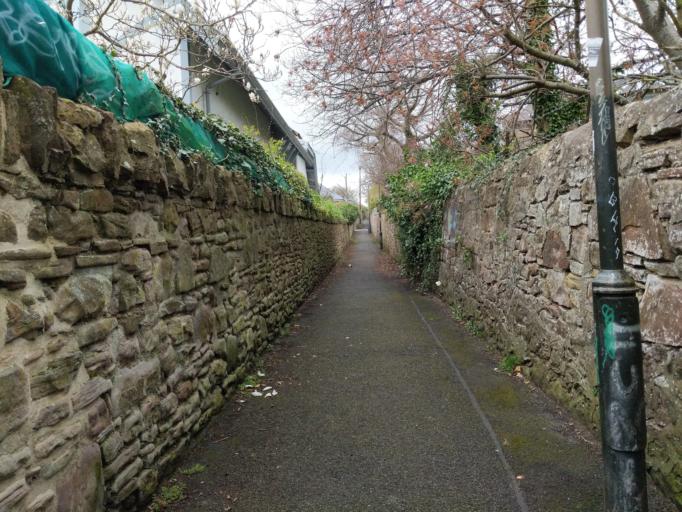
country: GB
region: Scotland
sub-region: Edinburgh
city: Edinburgh
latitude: 55.9328
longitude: -3.1878
